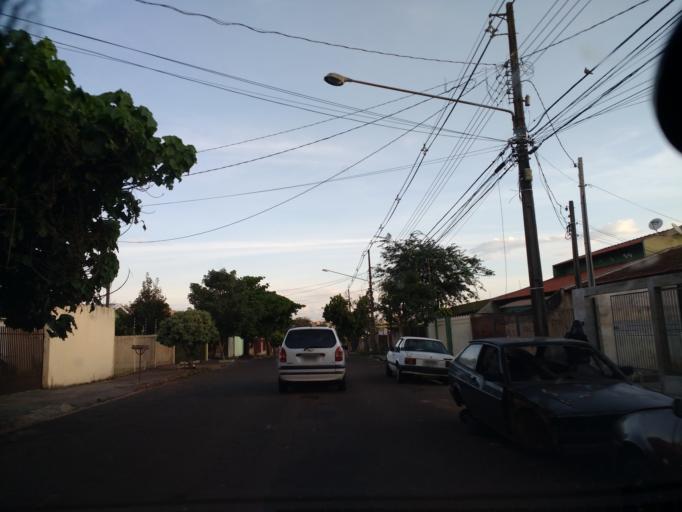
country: BR
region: Parana
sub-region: Londrina
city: Londrina
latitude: -23.2961
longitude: -51.1435
